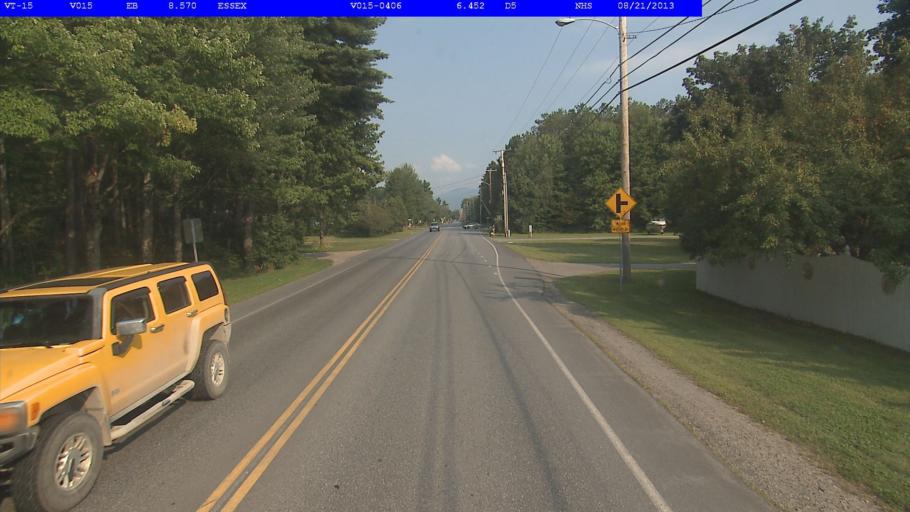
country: US
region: Vermont
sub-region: Chittenden County
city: Jericho
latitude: 44.5049
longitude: -73.0400
